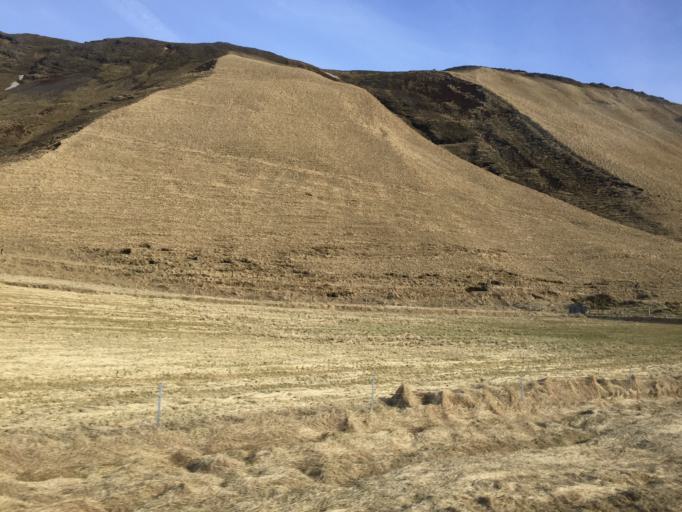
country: IS
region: South
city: Vestmannaeyjar
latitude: 63.4097
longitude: -19.0481
